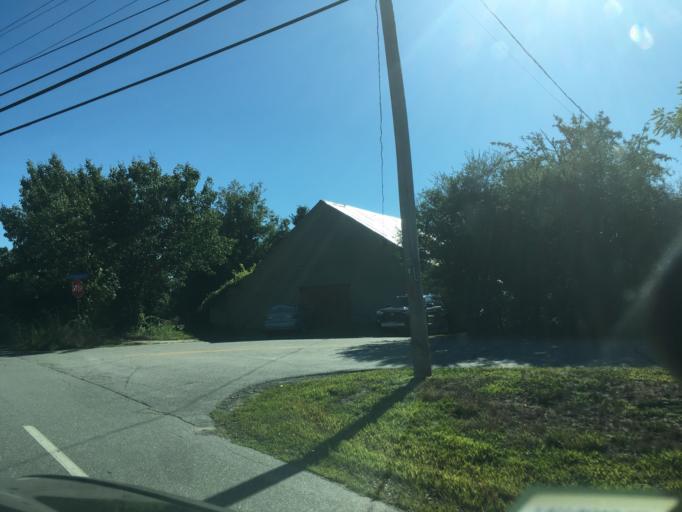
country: US
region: New Hampshire
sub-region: Rockingham County
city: Stratham Station
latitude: 43.0167
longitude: -70.9166
